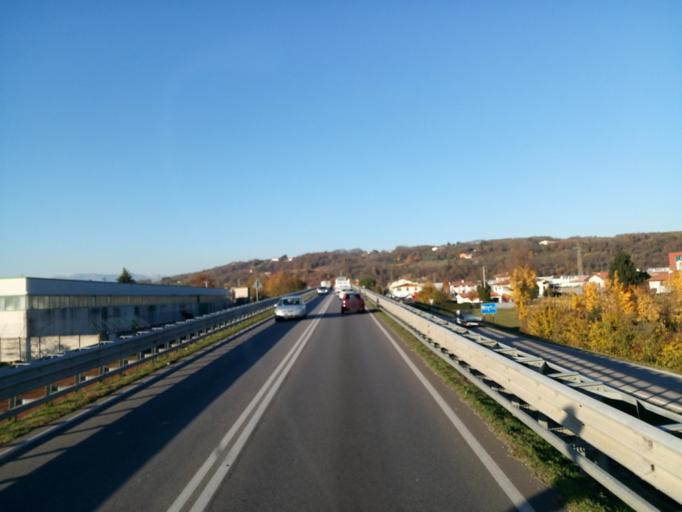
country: IT
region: Veneto
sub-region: Provincia di Treviso
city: Montebelluna
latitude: 45.7778
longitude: 12.0681
